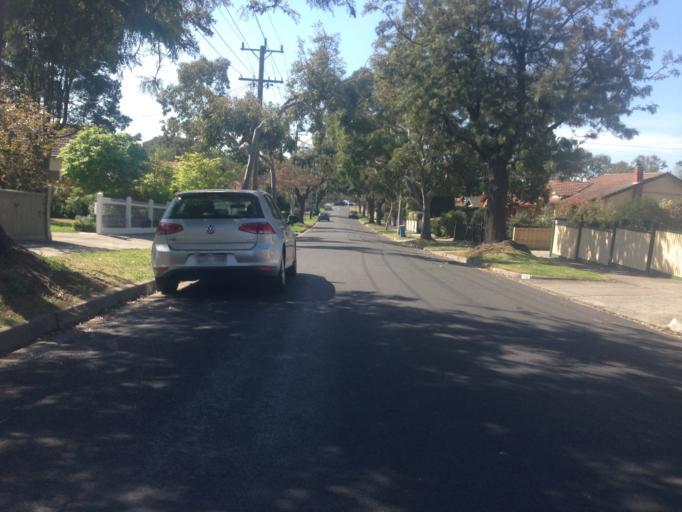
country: AU
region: Victoria
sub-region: Boroondara
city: Kew East
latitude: -37.7947
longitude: 145.0578
